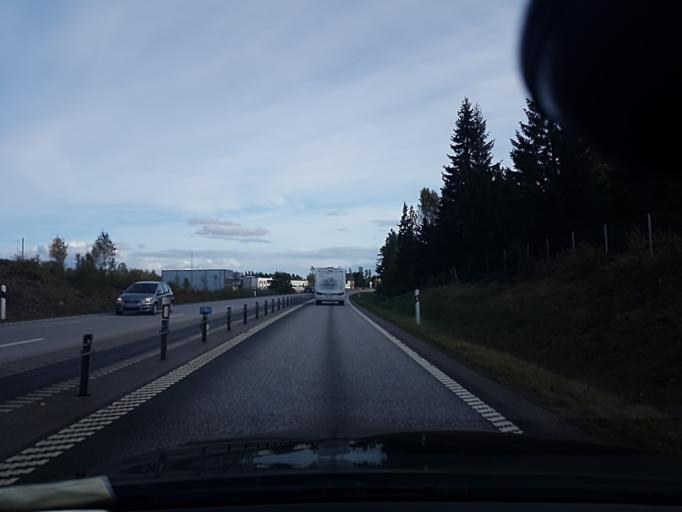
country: SE
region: Joenkoeping
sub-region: Varnamo Kommun
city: Varnamo
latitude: 57.1826
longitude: 13.9890
